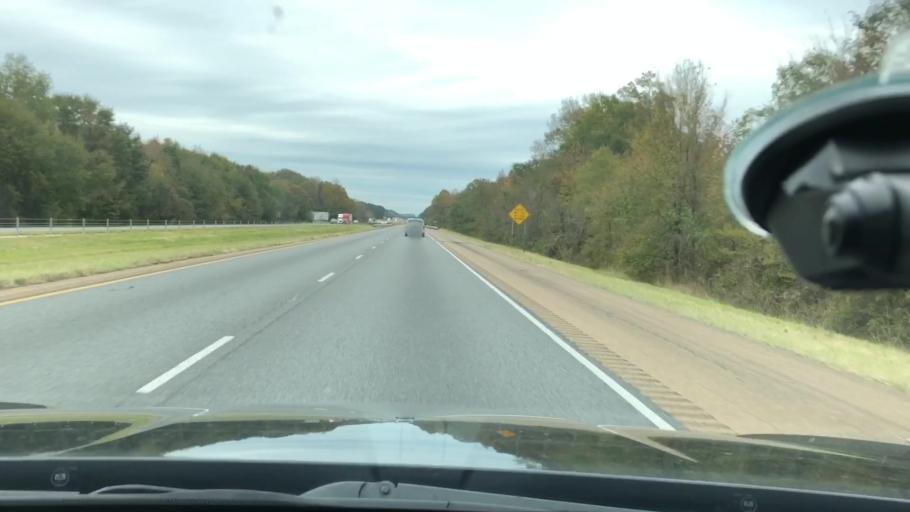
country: US
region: Arkansas
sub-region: Nevada County
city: Prescott
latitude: 33.8953
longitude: -93.3078
